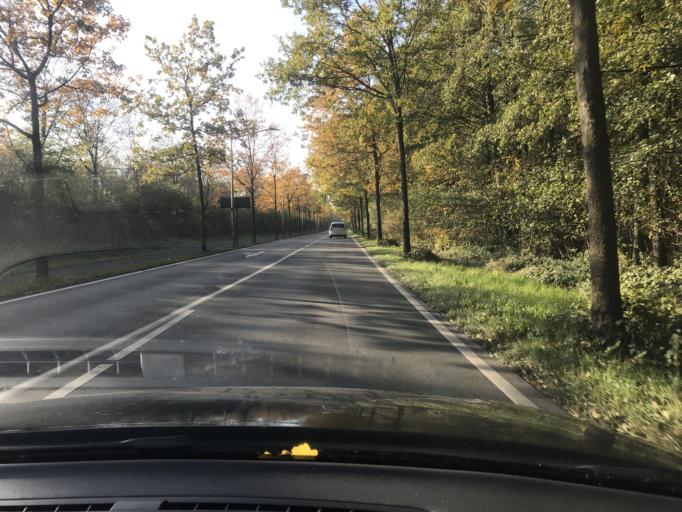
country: DE
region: North Rhine-Westphalia
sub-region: Regierungsbezirk Arnsberg
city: Hamm
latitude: 51.6597
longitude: 7.8510
